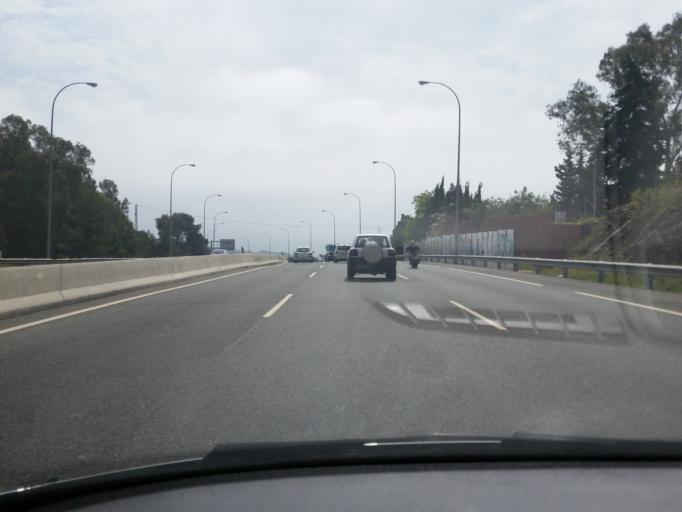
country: ES
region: Andalusia
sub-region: Provincia de Malaga
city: Malaga
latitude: 36.7461
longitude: -4.4082
